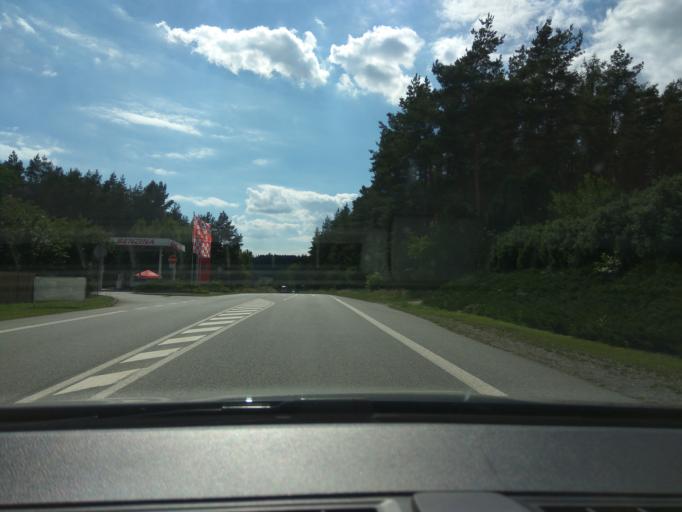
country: CZ
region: Jihocesky
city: Cimelice
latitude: 49.5026
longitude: 14.1592
